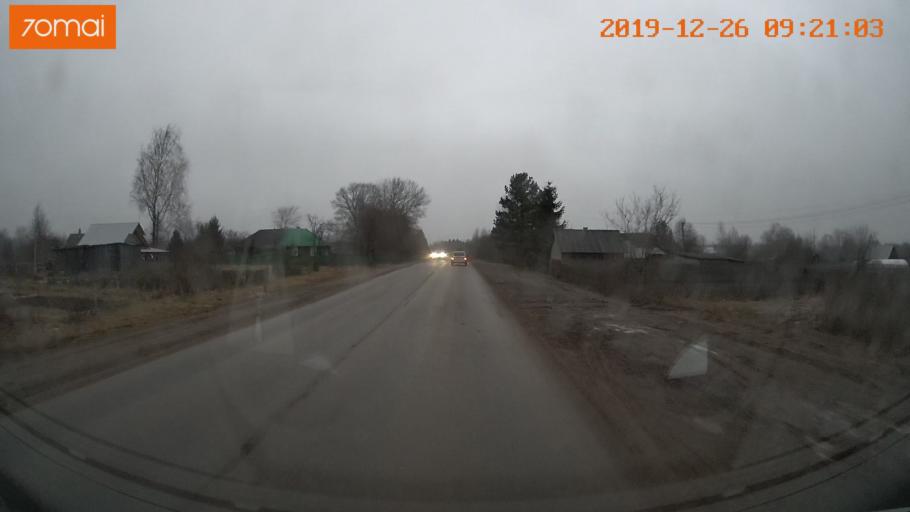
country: RU
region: Vologda
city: Gryazovets
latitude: 58.9669
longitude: 40.2266
